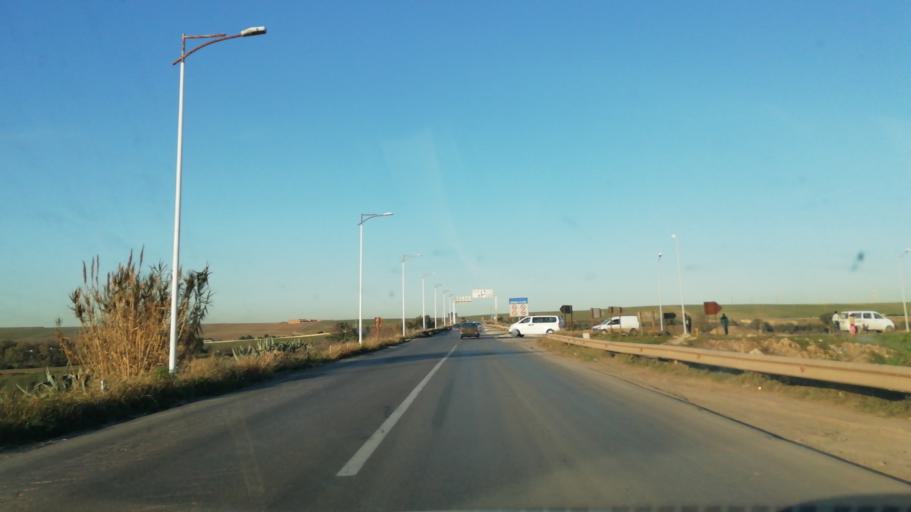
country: DZ
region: Oran
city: Sidi ech Chahmi
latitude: 35.5697
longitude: -0.5584
